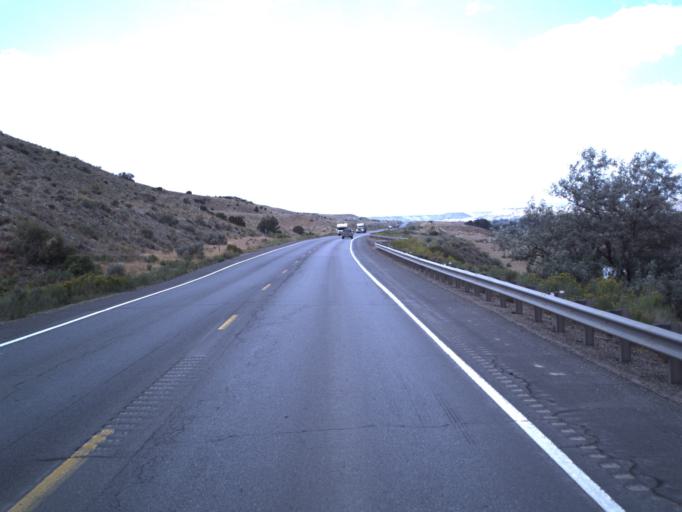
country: US
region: Utah
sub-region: Duchesne County
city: Duchesne
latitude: 40.1590
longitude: -110.2645
